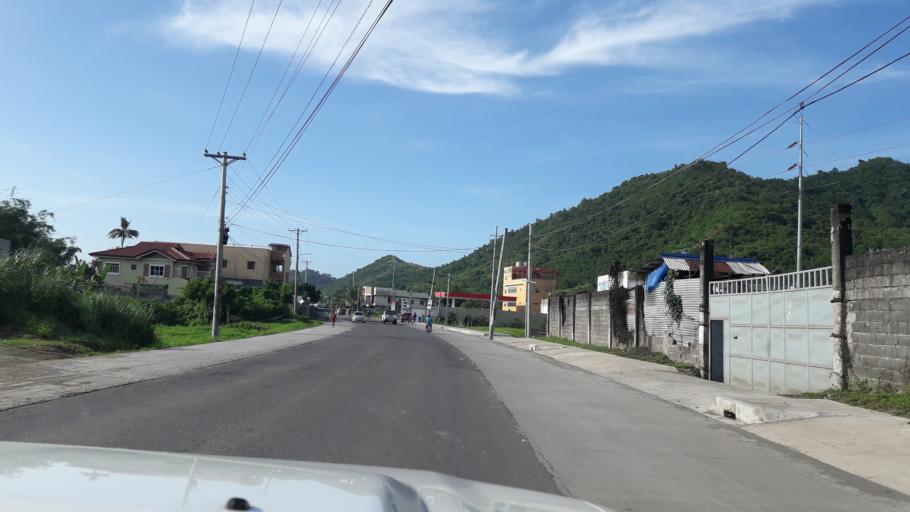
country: PH
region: Eastern Visayas
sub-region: Province of Leyte
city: Pawing
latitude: 11.2077
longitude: 124.9916
